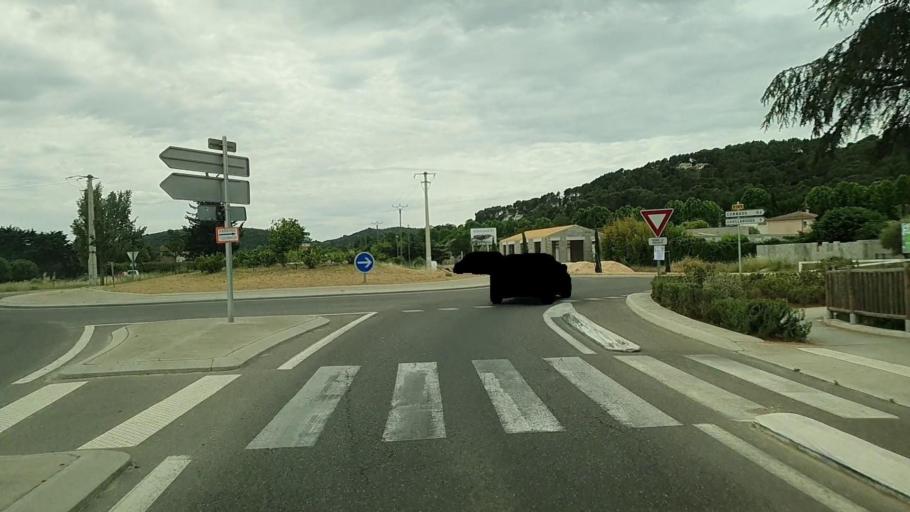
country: FR
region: Languedoc-Roussillon
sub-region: Departement du Gard
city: Connaux
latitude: 44.0879
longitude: 4.5953
